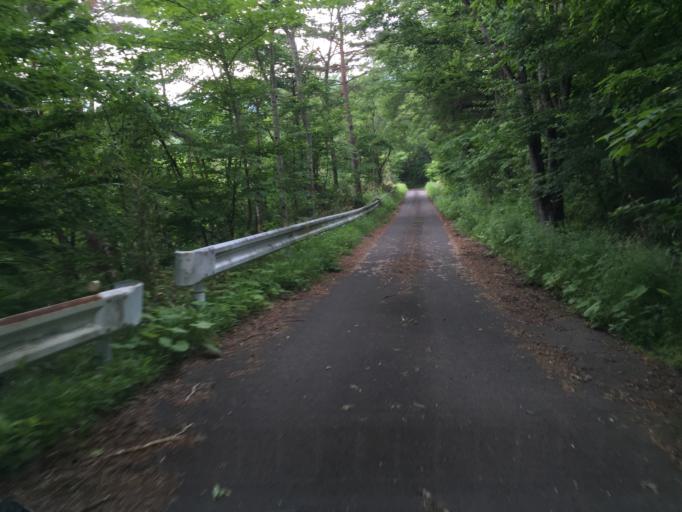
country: JP
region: Fukushima
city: Fukushima-shi
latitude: 37.7196
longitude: 140.3377
